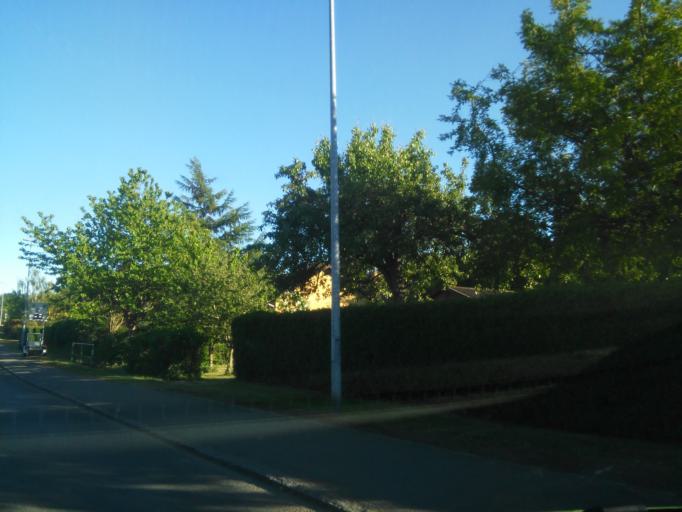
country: DK
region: Capital Region
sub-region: Bornholm Kommune
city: Ronne
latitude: 55.2704
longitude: 14.8017
